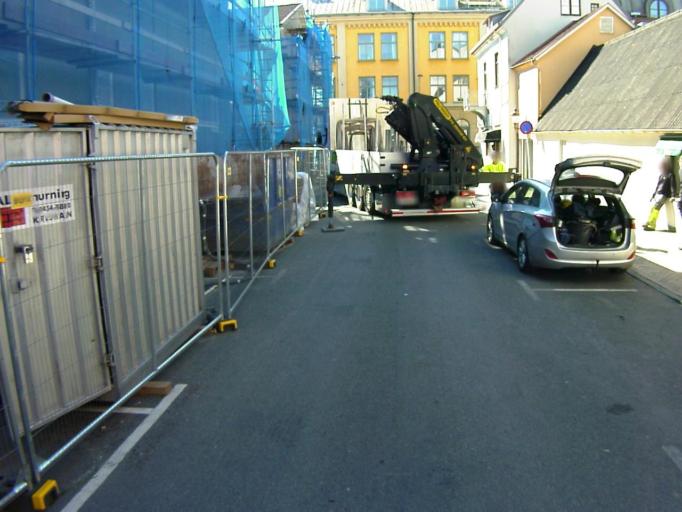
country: SE
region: Skane
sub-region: Kristianstads Kommun
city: Kristianstad
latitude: 56.0290
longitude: 14.1587
